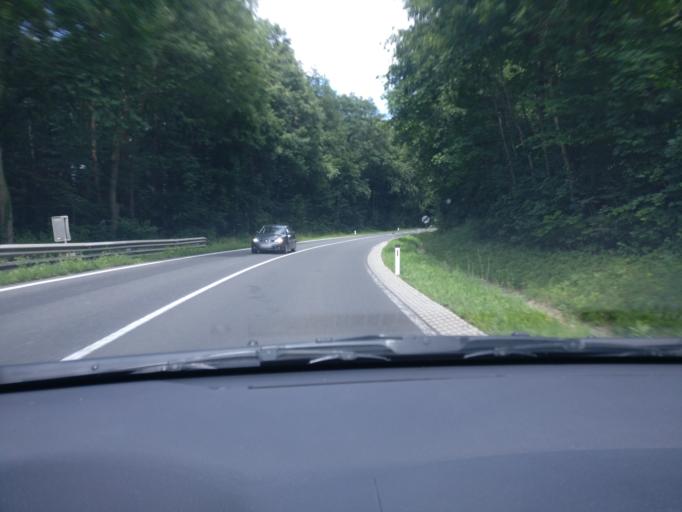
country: AT
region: Styria
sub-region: Politischer Bezirk Hartberg-Fuerstenfeld
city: Kaibing
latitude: 47.2047
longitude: 15.8426
